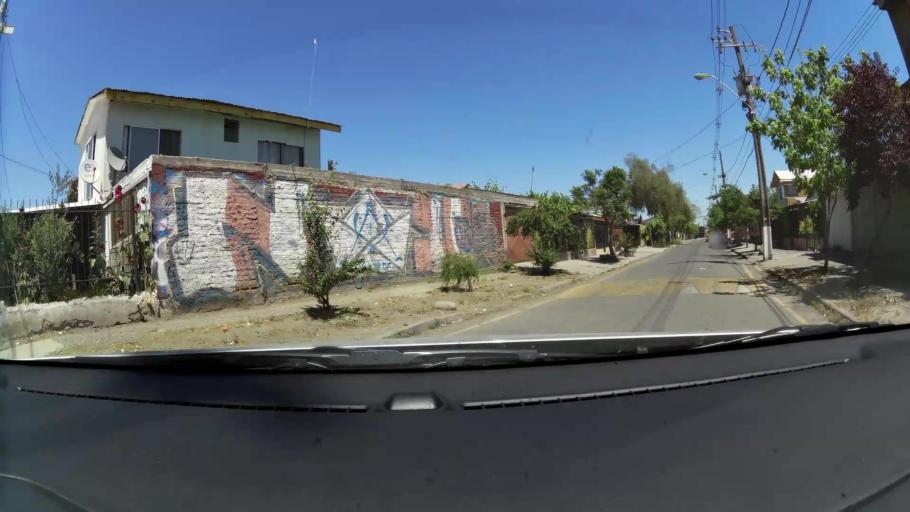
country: CL
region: Santiago Metropolitan
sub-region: Provincia de Santiago
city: La Pintana
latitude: -33.5721
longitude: -70.6619
